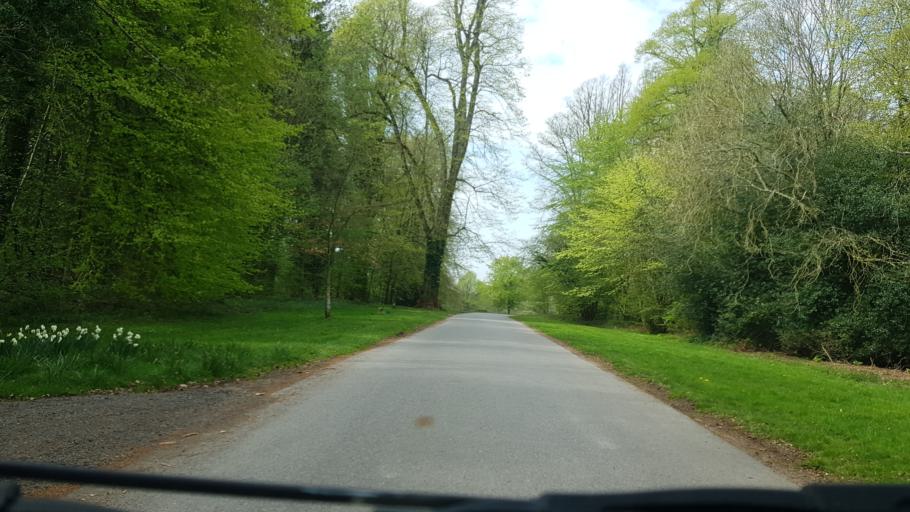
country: GB
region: England
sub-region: Hampshire
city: Highclere
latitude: 51.3287
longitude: -1.3488
